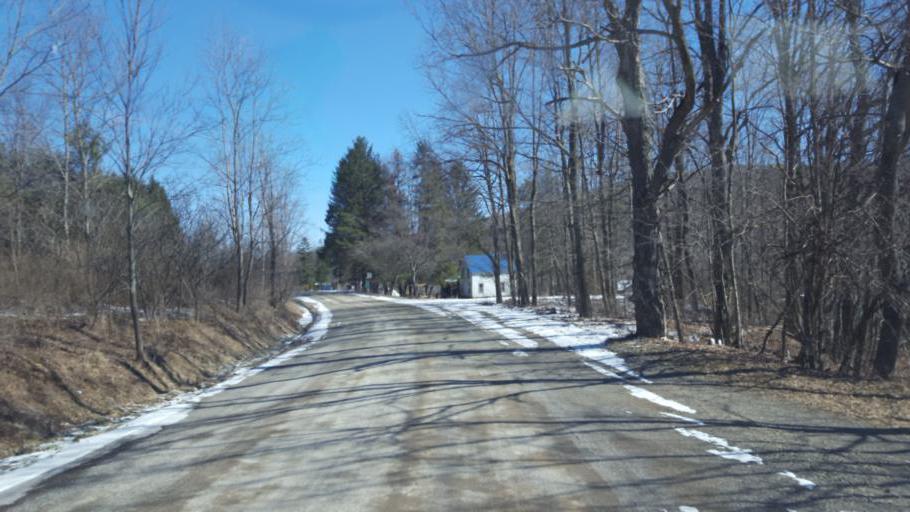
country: US
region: New York
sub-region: Allegany County
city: Wellsville
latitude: 42.0521
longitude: -77.9571
